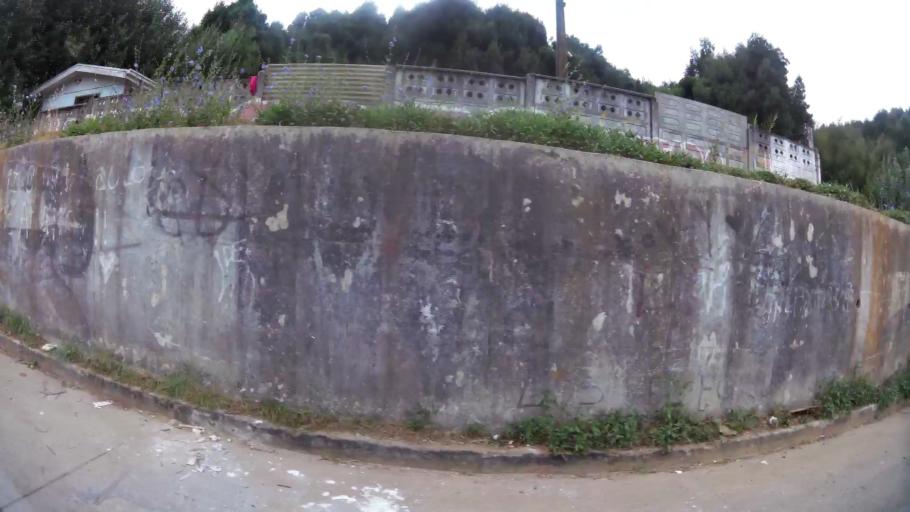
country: CL
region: Biobio
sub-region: Provincia de Concepcion
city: Concepcion
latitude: -36.8345
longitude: -73.0000
